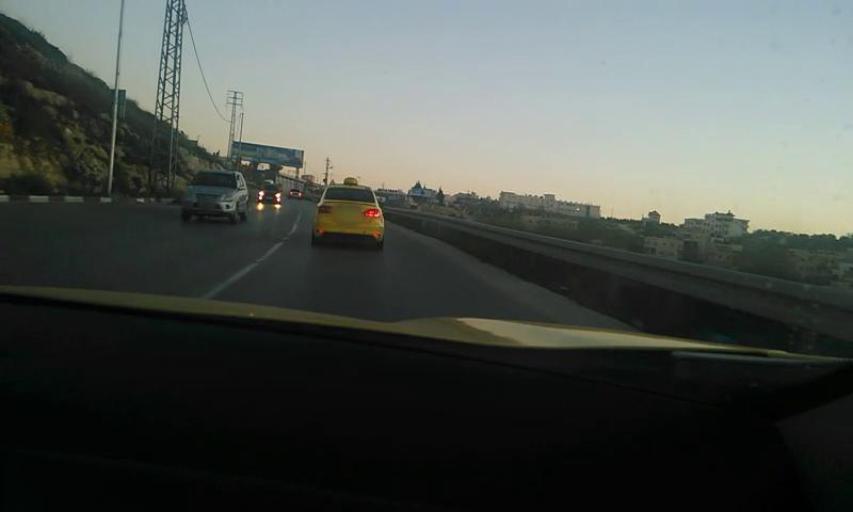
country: PS
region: West Bank
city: Jifna
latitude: 31.9493
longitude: 35.2153
